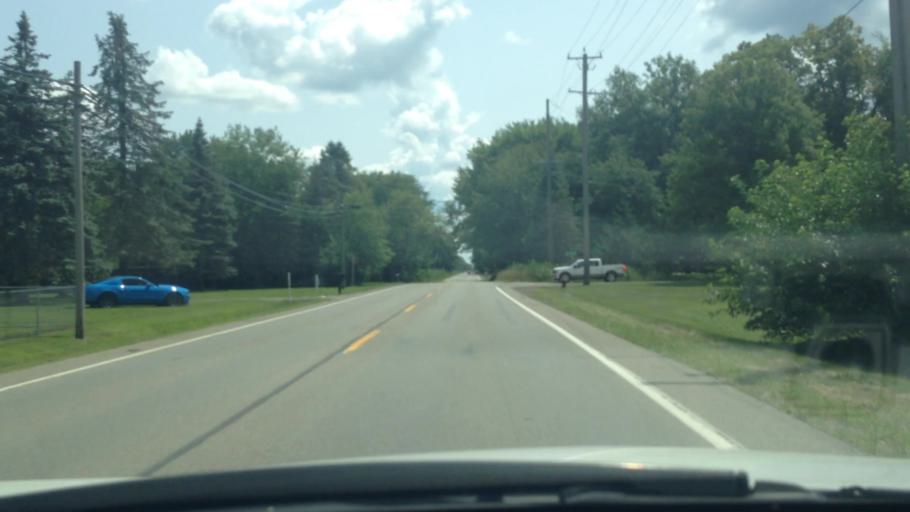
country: US
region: Michigan
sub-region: Wayne County
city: Taylor
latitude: 42.1782
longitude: -83.3060
